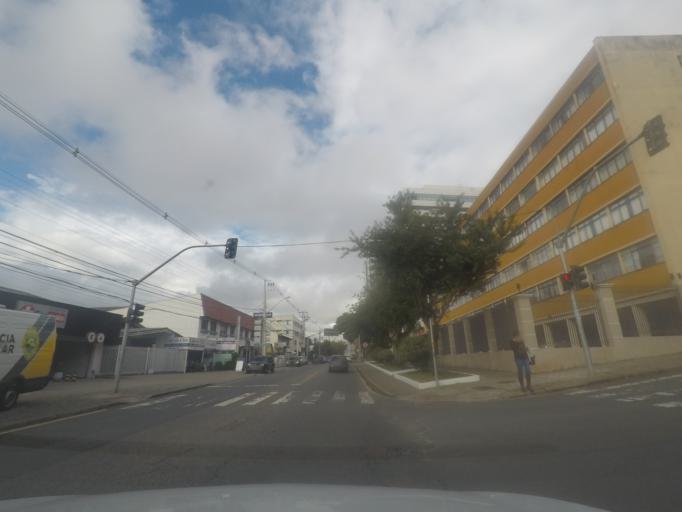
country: BR
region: Parana
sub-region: Curitiba
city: Curitiba
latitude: -25.4353
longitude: -49.2443
